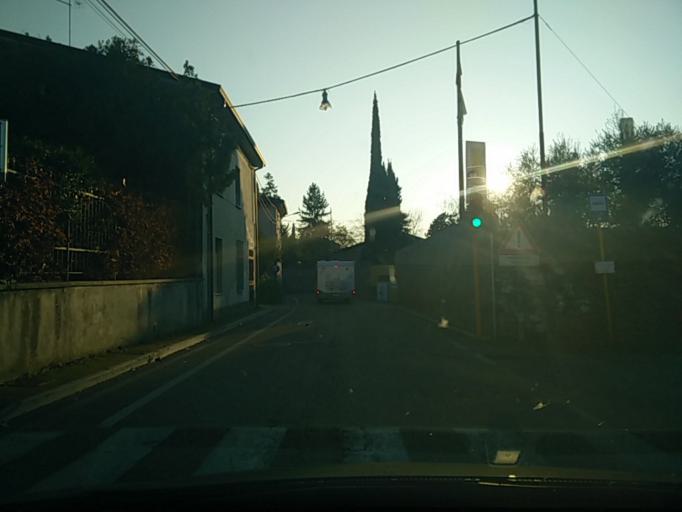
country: IT
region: Veneto
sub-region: Provincia di Verona
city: Salionze
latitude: 45.4022
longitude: 10.7210
